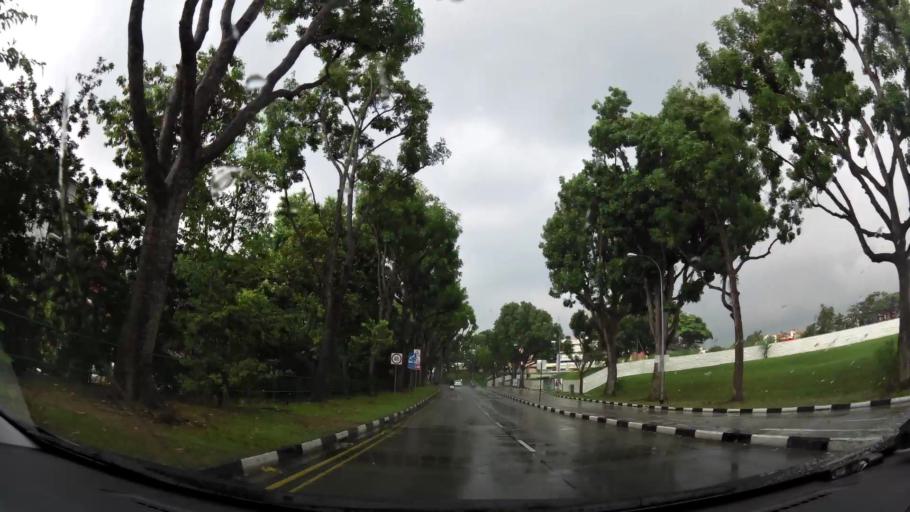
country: SG
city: Singapore
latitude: 1.3394
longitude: 103.9594
